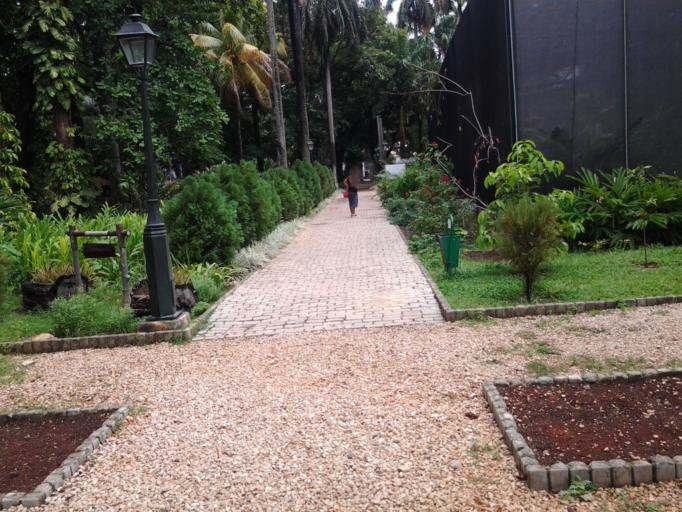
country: CU
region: La Habana
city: Havana
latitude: 23.1321
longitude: -82.3793
